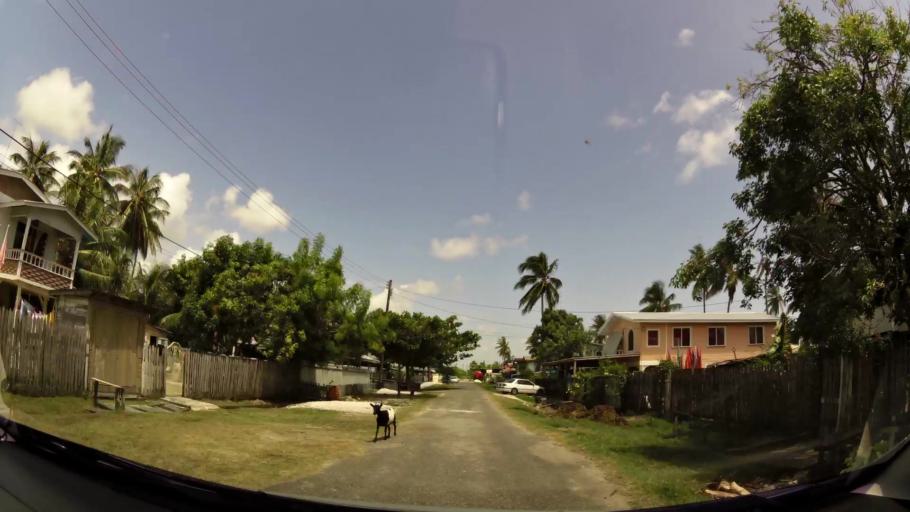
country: GY
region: Demerara-Mahaica
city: Mahaica Village
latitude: 6.7680
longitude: -58.0087
